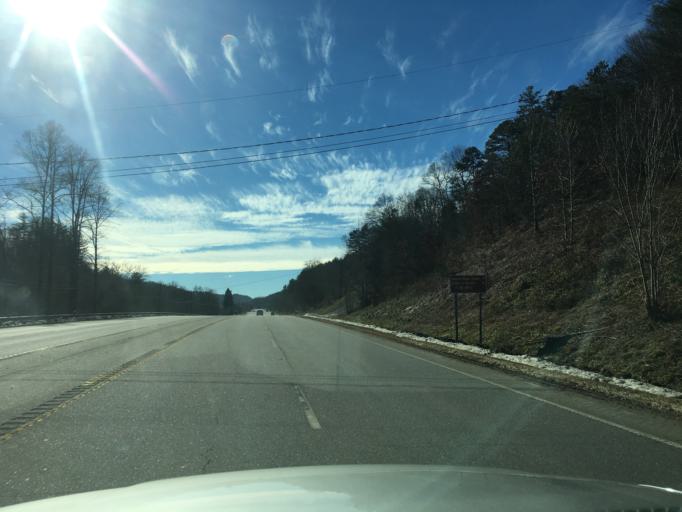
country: US
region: North Carolina
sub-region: Henderson County
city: Etowah
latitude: 35.3252
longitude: -82.6518
